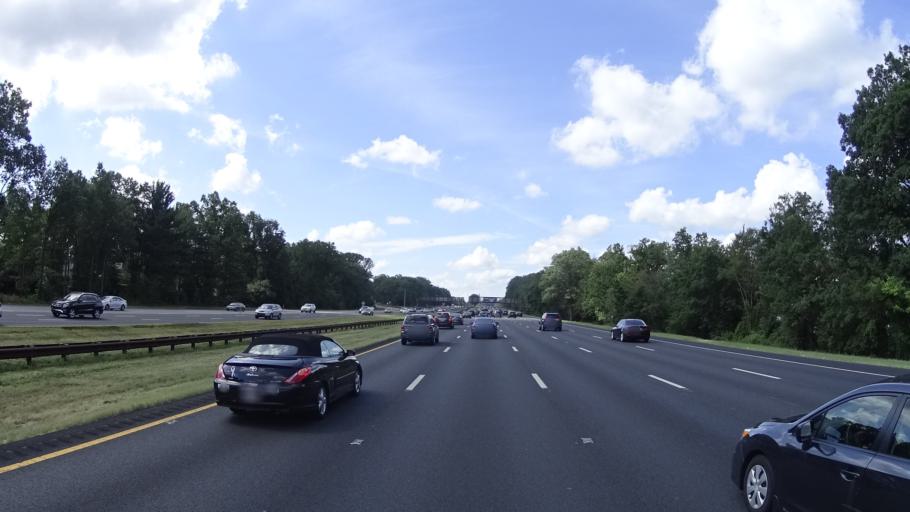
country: US
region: New Jersey
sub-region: Middlesex County
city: Iselin
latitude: 40.5956
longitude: -74.3215
